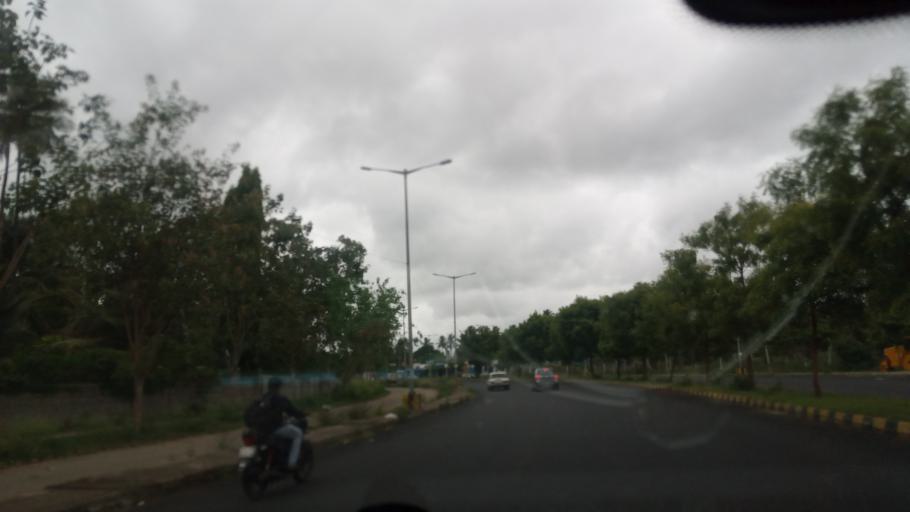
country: IN
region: Karnataka
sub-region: Mysore
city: Mysore
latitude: 12.3069
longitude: 76.6014
